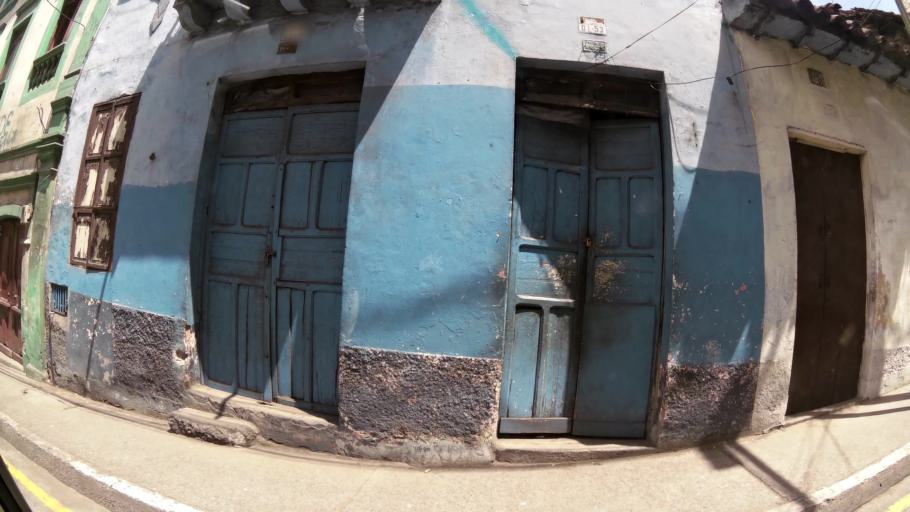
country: EC
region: Tungurahua
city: Ambato
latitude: -1.2447
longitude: -78.6262
